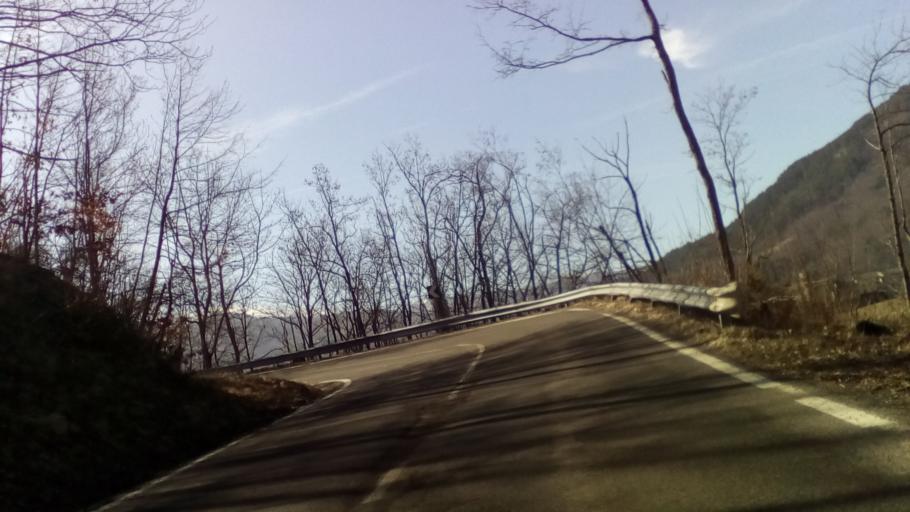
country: IT
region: Emilia-Romagna
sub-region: Provincia di Modena
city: Pievepelago
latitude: 44.2174
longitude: 10.6171
